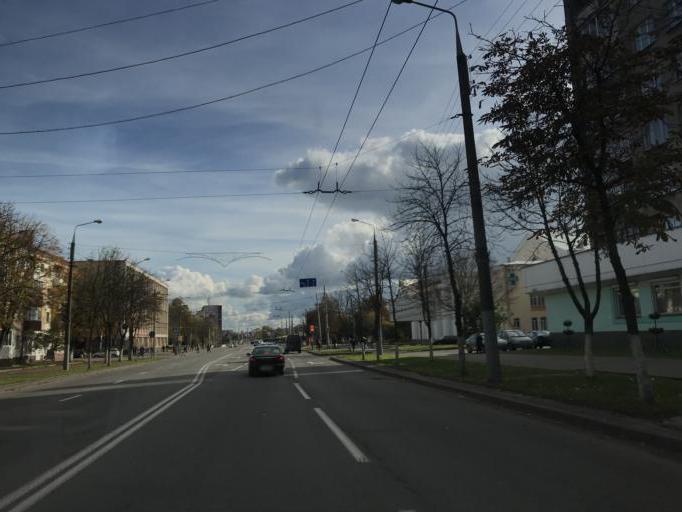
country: BY
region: Gomel
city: Gomel
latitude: 52.4493
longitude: 30.9678
